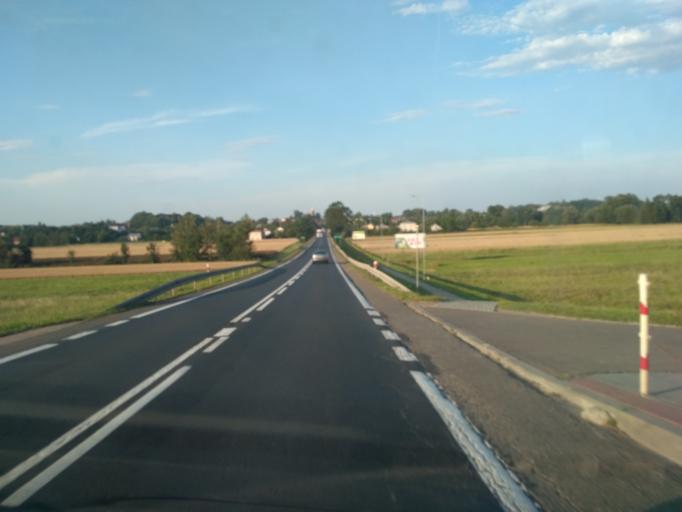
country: PL
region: Subcarpathian Voivodeship
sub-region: Powiat krosnienski
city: Miejsce Piastowe
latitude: 49.6266
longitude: 21.7727
